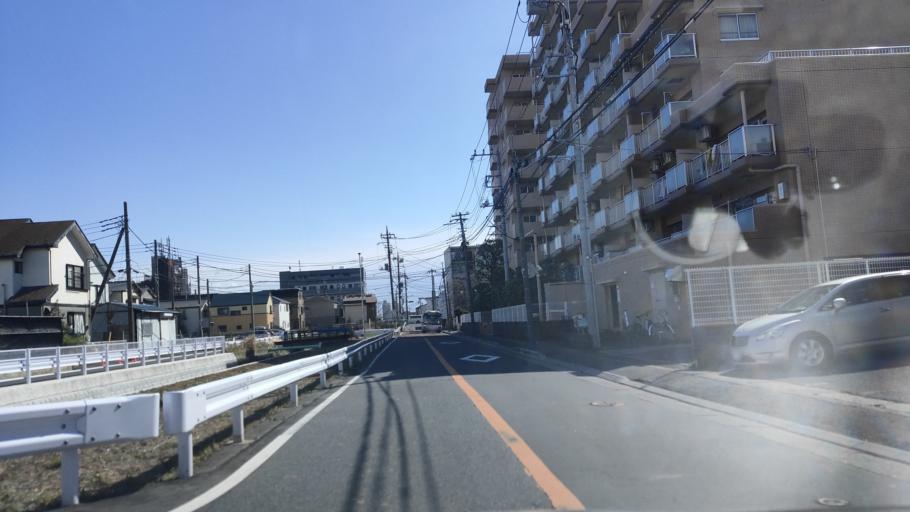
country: JP
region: Chiba
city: Matsudo
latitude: 35.7460
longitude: 139.9243
